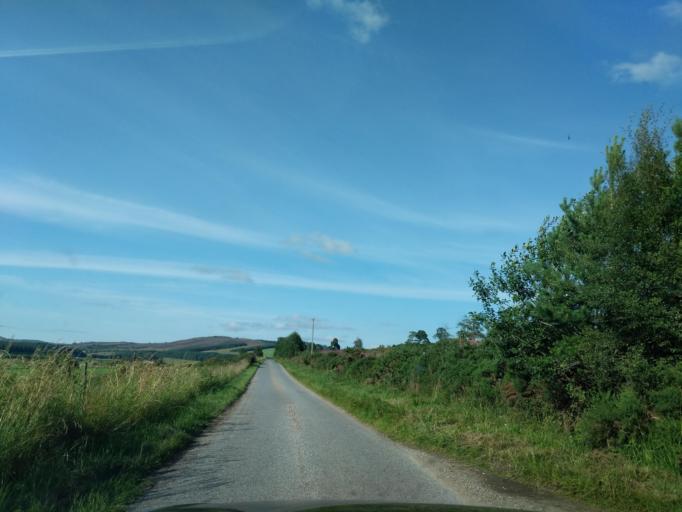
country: GB
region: Scotland
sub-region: Highland
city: Grantown on Spey
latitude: 57.2925
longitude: -3.7157
